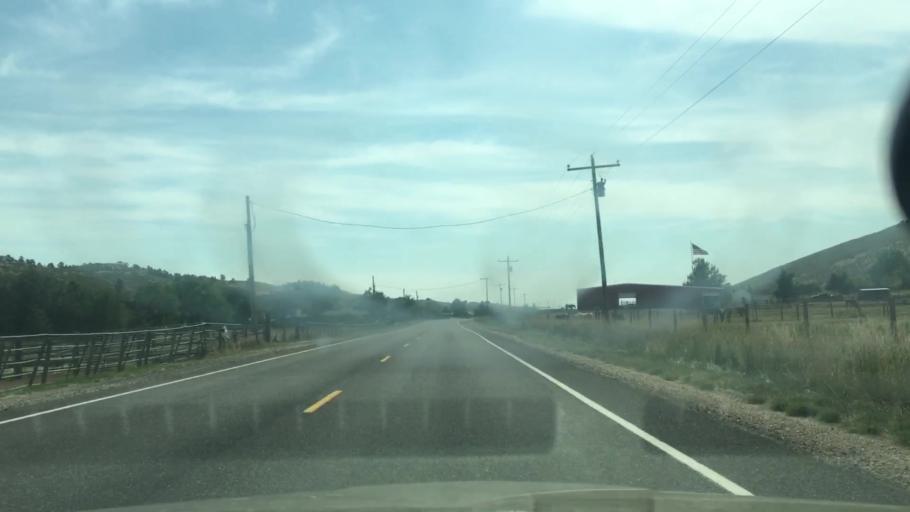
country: US
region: Colorado
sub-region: Larimer County
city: Campion
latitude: 40.3694
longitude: -105.1902
